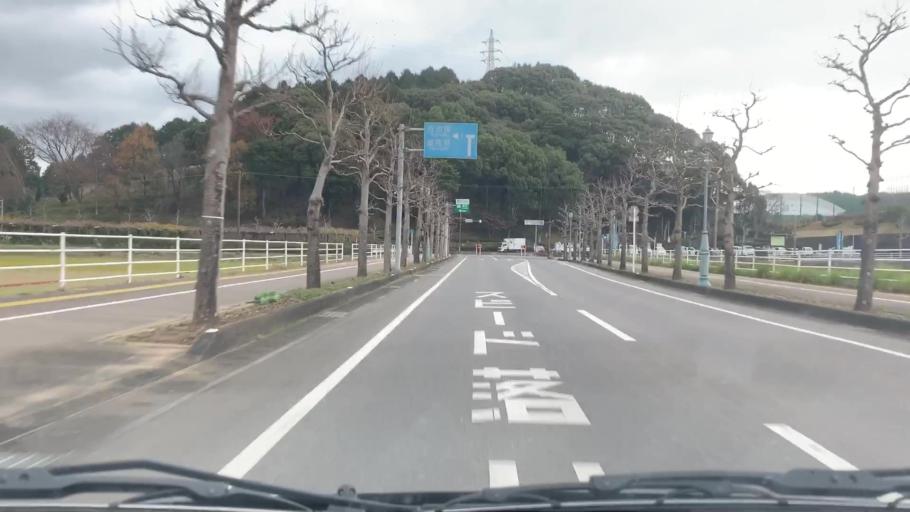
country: JP
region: Saga Prefecture
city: Ureshinomachi-shimojuku
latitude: 33.1071
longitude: 129.9847
